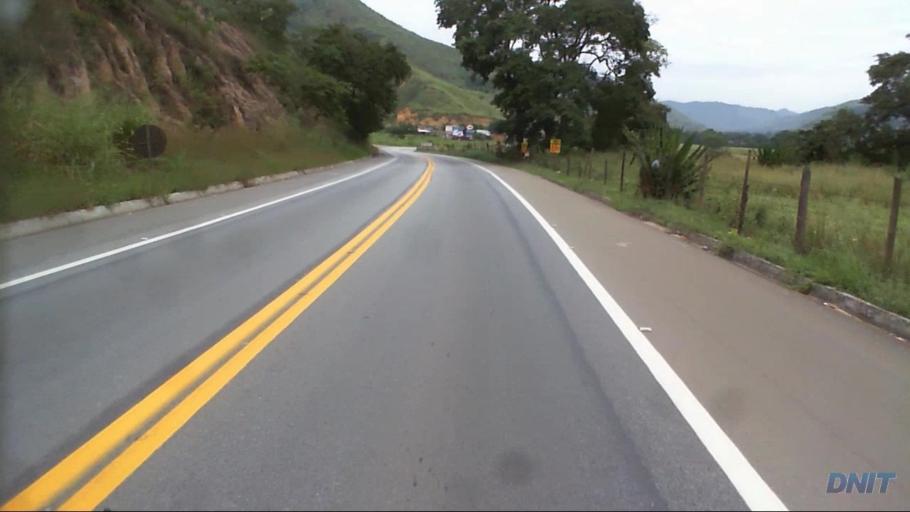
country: BR
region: Minas Gerais
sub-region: Timoteo
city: Timoteo
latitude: -19.5822
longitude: -42.7277
